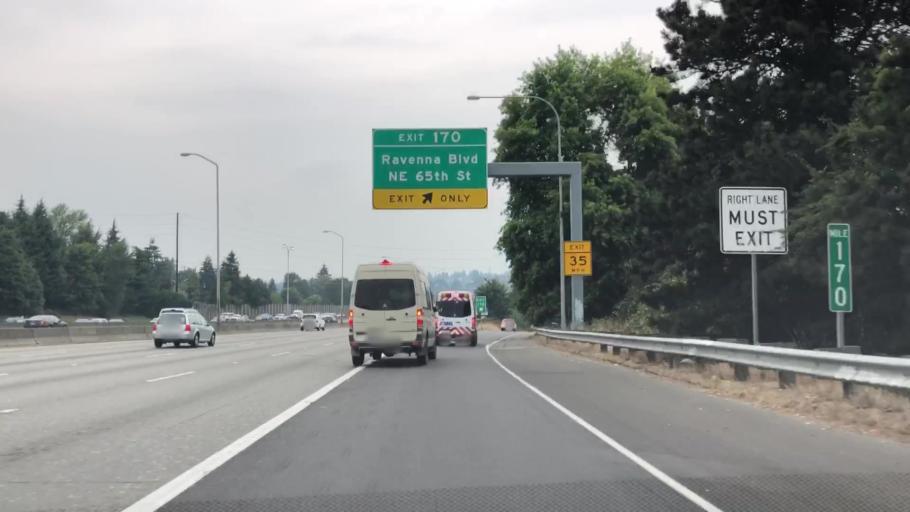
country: US
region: Washington
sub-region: King County
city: Seattle
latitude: 47.6703
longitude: -122.3215
